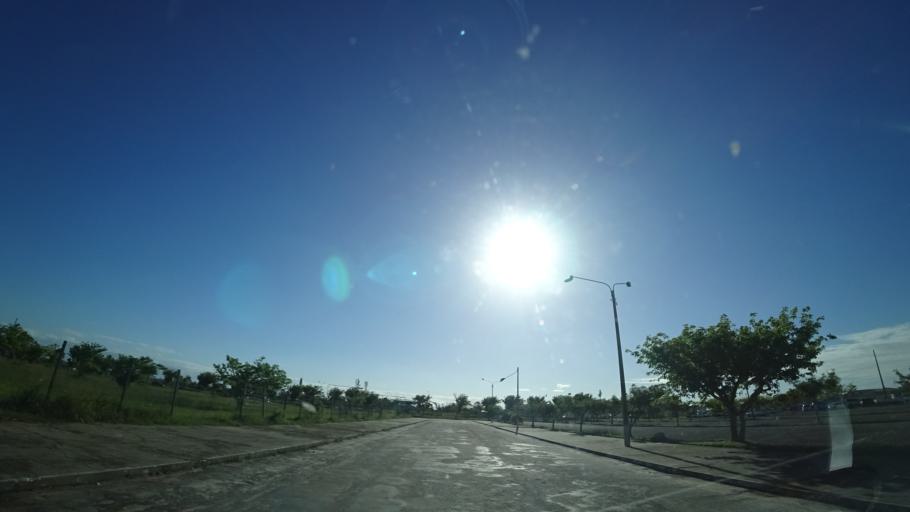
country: MZ
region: Sofala
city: Beira
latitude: -19.7996
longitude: 34.9016
